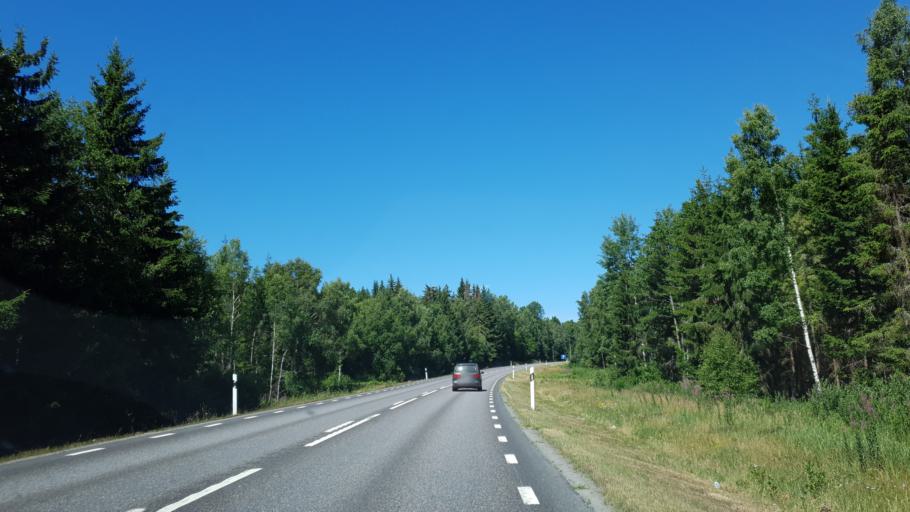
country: SE
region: Joenkoeping
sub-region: Varnamo Kommun
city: Bor
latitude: 57.0633
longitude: 14.1869
